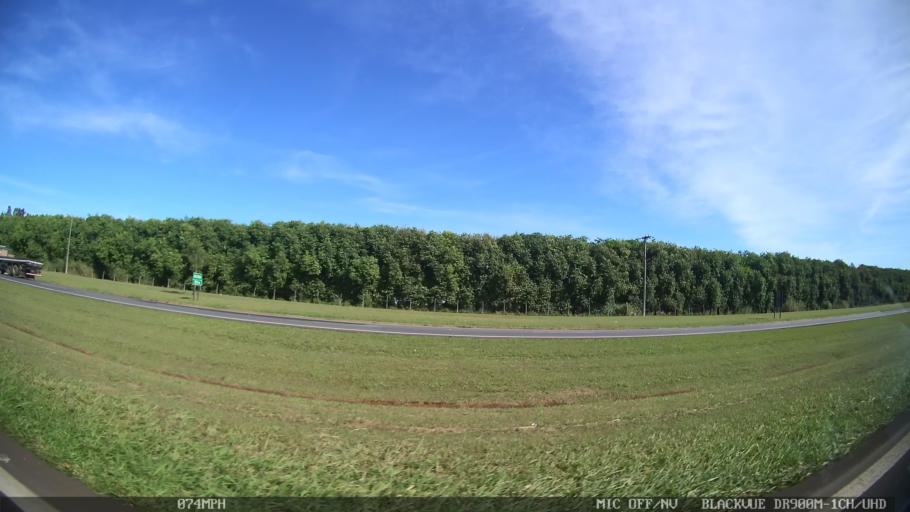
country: BR
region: Sao Paulo
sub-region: Cordeiropolis
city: Cordeiropolis
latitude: -22.4587
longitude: -47.3987
